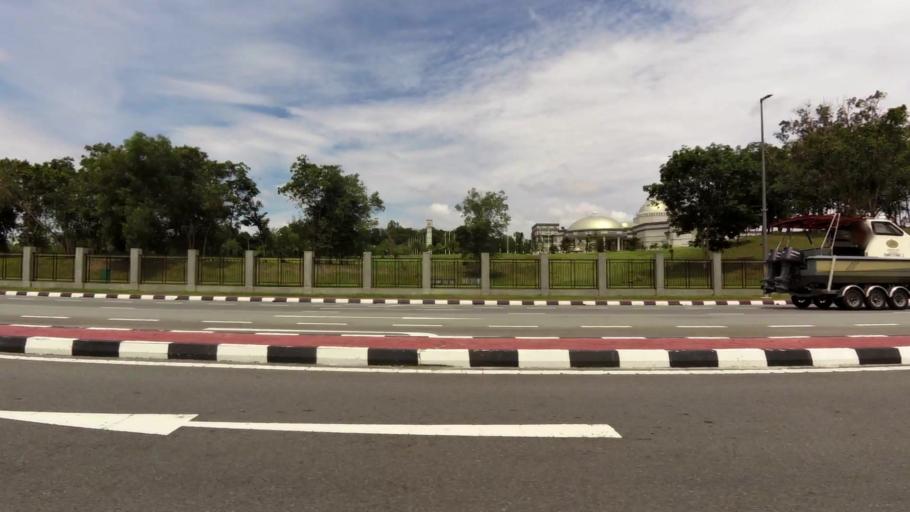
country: BN
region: Brunei and Muara
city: Bandar Seri Begawan
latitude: 4.9224
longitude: 114.9361
